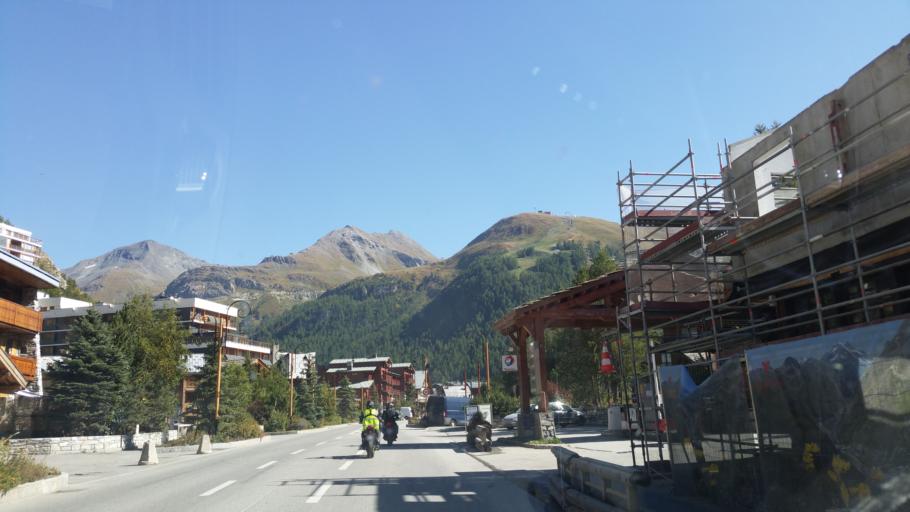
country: FR
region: Rhone-Alpes
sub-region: Departement de la Savoie
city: Val-d'Isere
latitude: 45.4535
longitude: 6.9723
